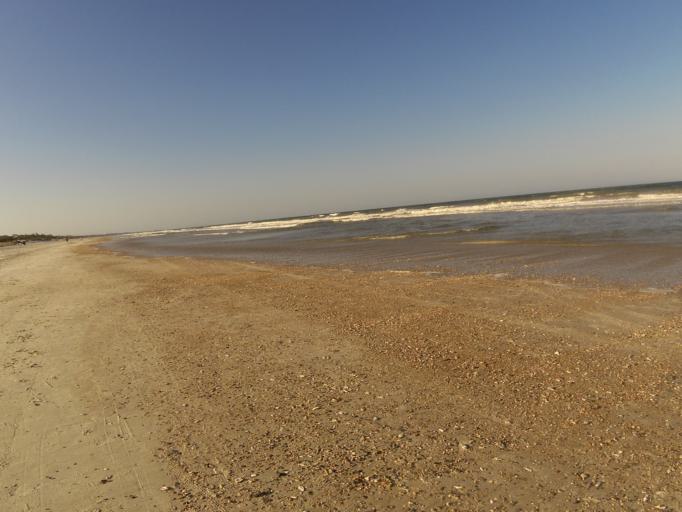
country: US
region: Florida
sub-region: Duval County
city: Atlantic Beach
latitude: 30.3514
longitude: -81.3970
